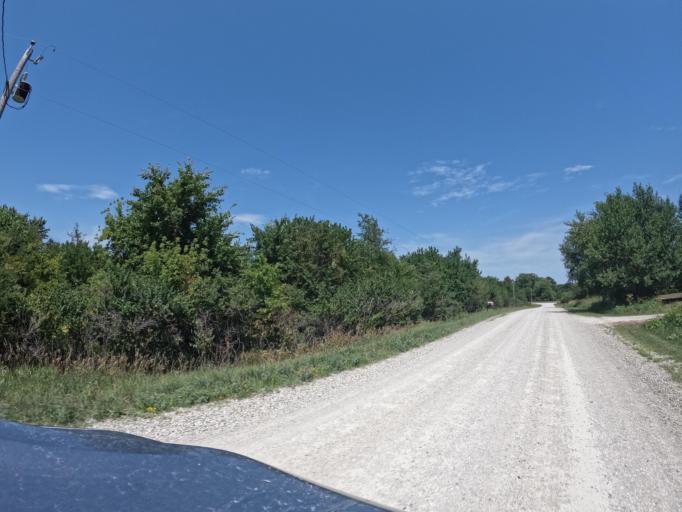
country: US
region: Iowa
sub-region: Henry County
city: Mount Pleasant
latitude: 40.8938
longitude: -91.6245
